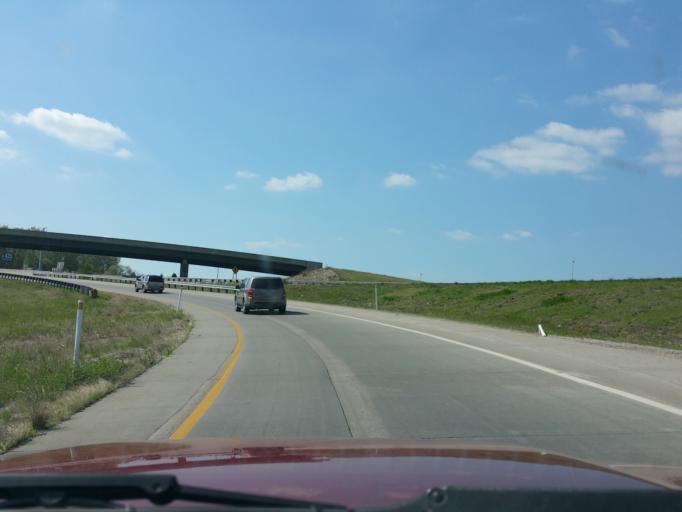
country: US
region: Kansas
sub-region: Wyandotte County
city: Kansas City
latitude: 39.1049
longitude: -94.6784
